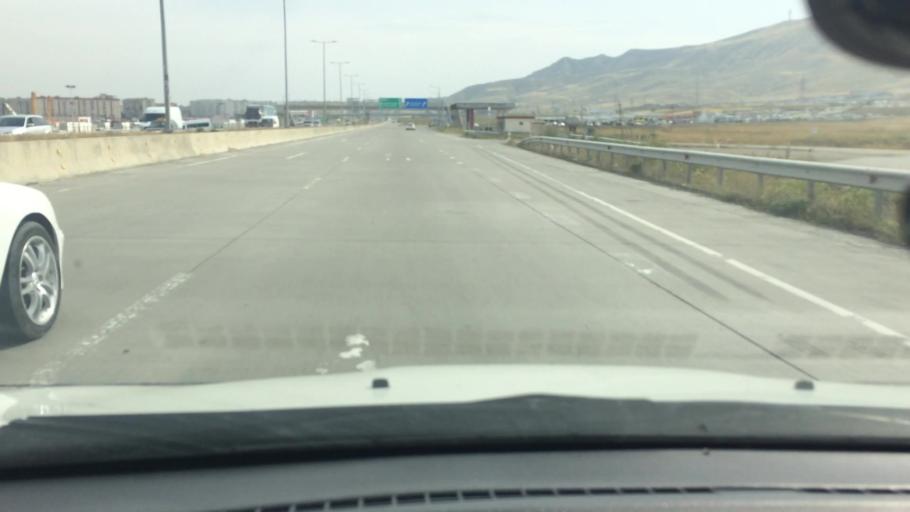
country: GE
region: Kvemo Kartli
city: Rust'avi
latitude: 41.5780
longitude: 44.9552
